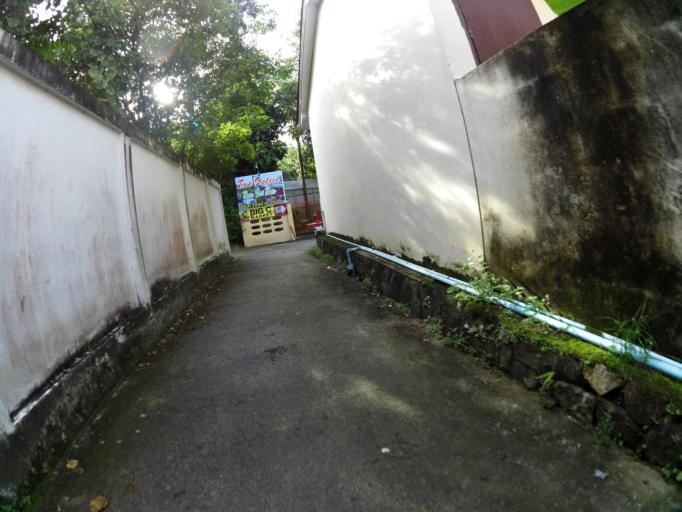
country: TH
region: Phuket
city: Patong
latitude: 7.9505
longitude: 98.2816
